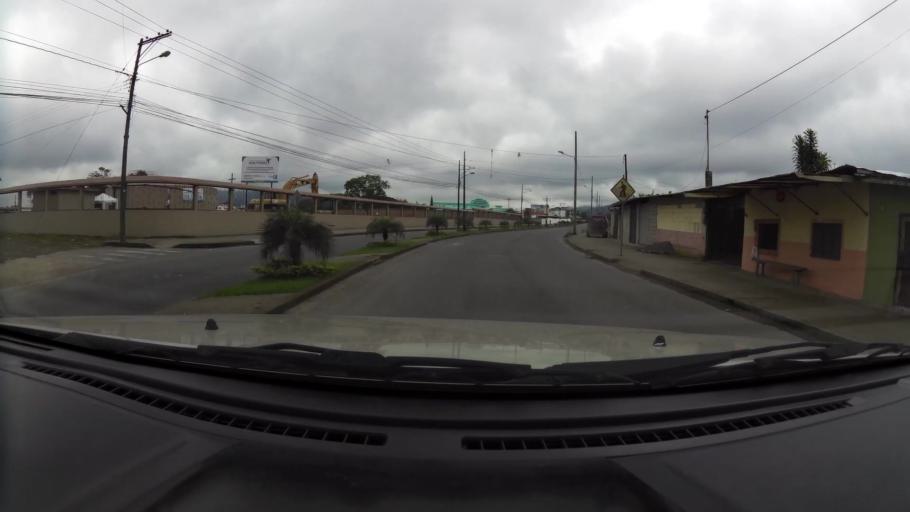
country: EC
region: Santo Domingo de los Tsachilas
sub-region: Canton Santo Domingo de los Colorados
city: Santo Domingo de los Colorados
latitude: -0.2585
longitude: -79.1444
